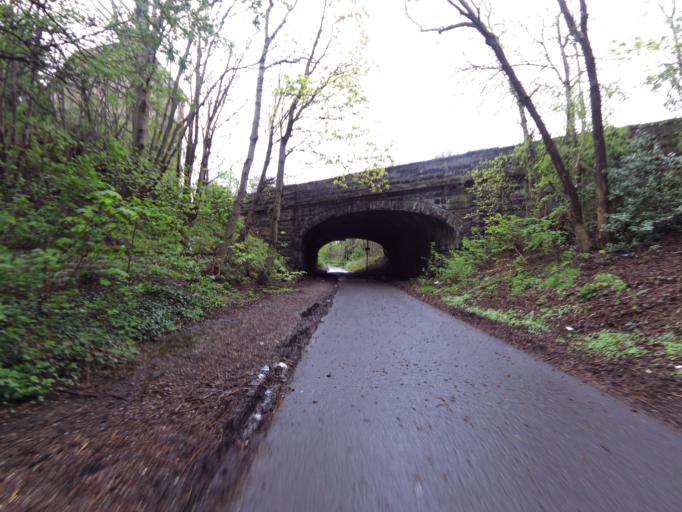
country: GB
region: Scotland
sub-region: Edinburgh
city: Edinburgh
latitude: 55.9568
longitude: -3.2445
